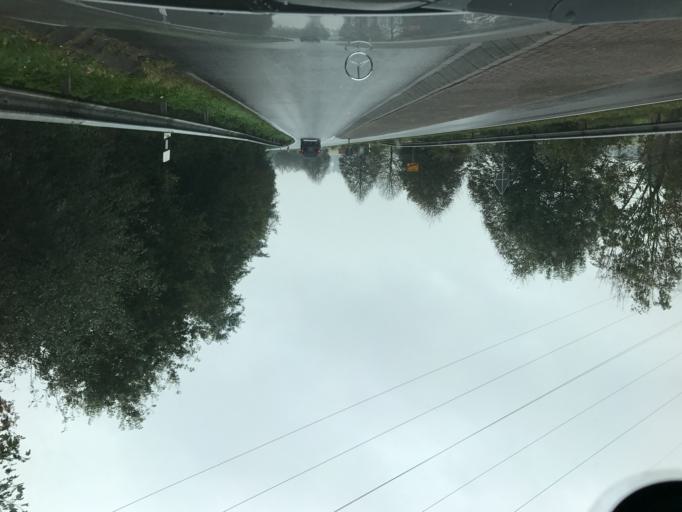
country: DE
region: Lower Saxony
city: Weener
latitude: 53.1285
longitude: 7.3188
